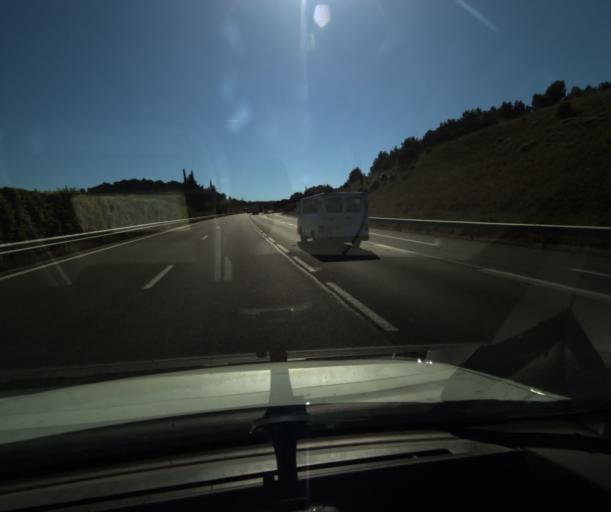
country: FR
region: Languedoc-Roussillon
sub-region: Departement de l'Aude
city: Cazilhac
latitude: 43.1923
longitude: 2.3668
